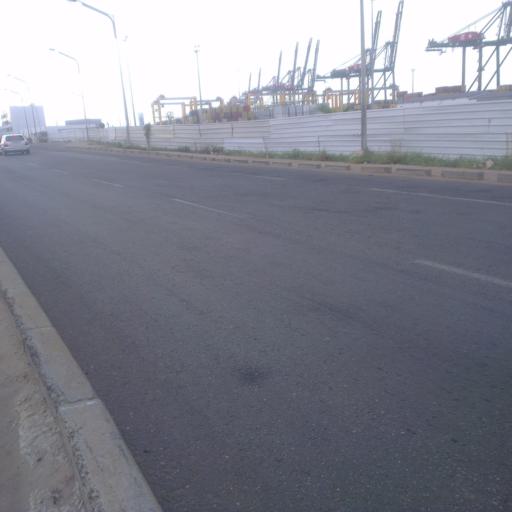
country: TG
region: Maritime
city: Lome
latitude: 6.1393
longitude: 1.2715
